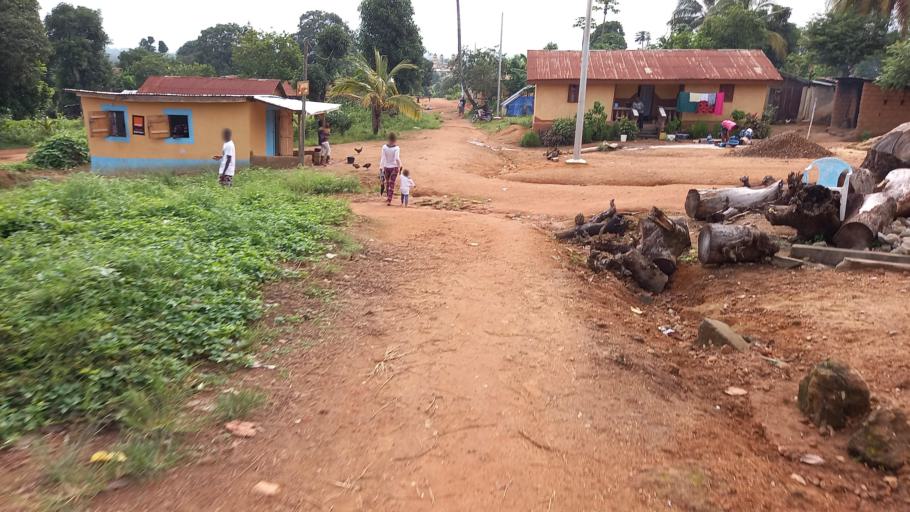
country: SL
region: Eastern Province
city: Kailahun
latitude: 8.2772
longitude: -10.5777
